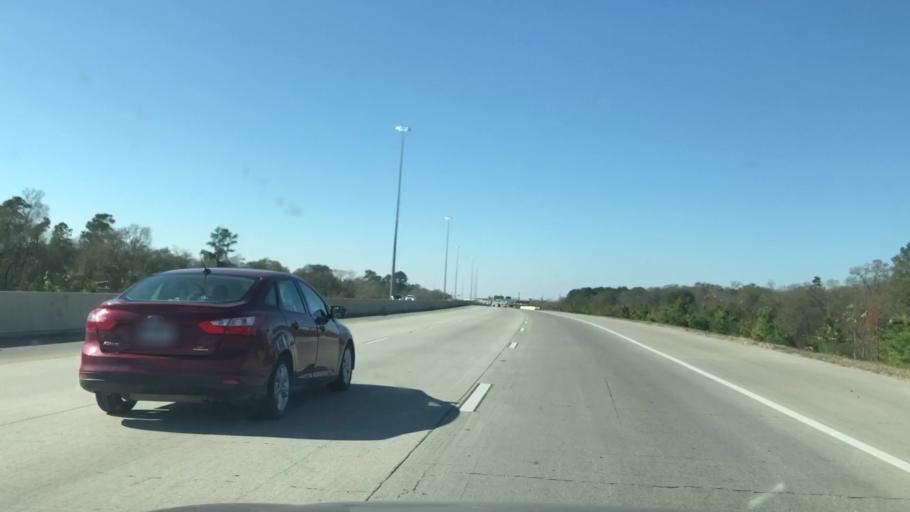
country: US
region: Texas
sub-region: Harris County
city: Jacinto City
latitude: 29.7910
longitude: -95.2368
